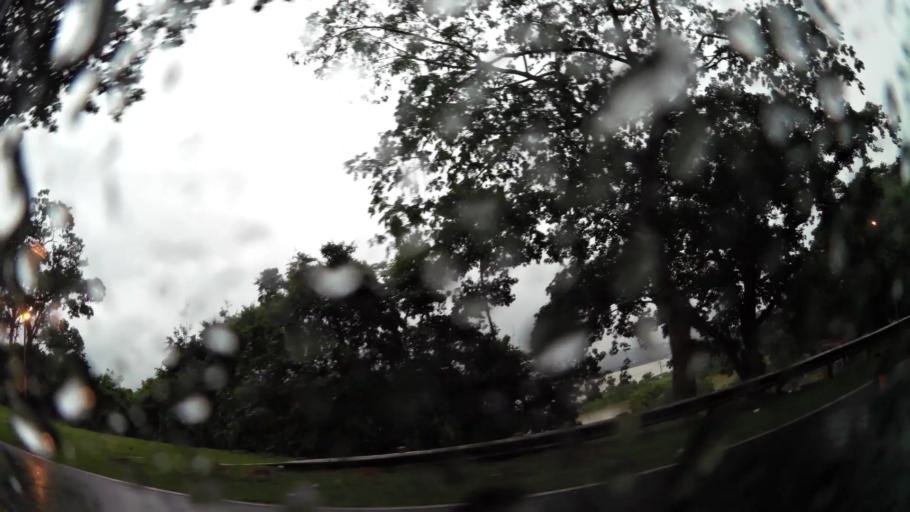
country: PA
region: Panama
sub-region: Distrito de Panama
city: Paraiso
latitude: 9.0084
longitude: -79.5955
